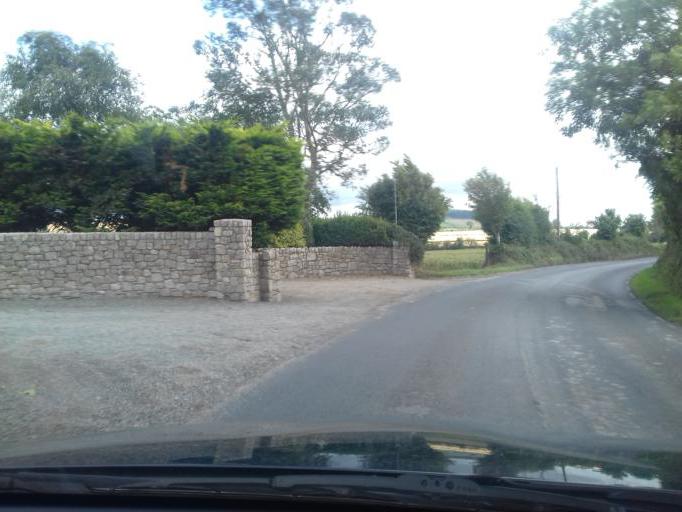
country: IE
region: Leinster
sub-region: Loch Garman
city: Ballinroad
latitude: 52.4901
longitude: -6.4648
